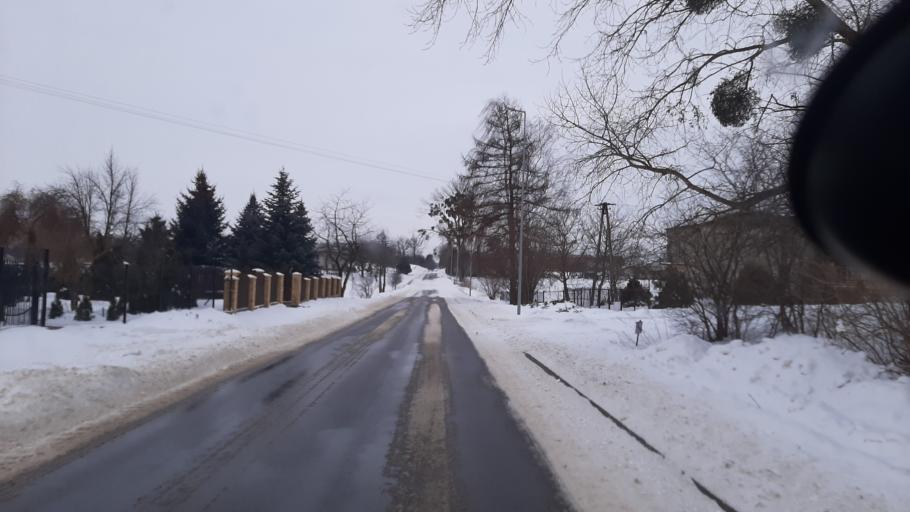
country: PL
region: Lublin Voivodeship
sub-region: Powiat lubelski
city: Garbow
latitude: 51.3251
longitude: 22.3253
